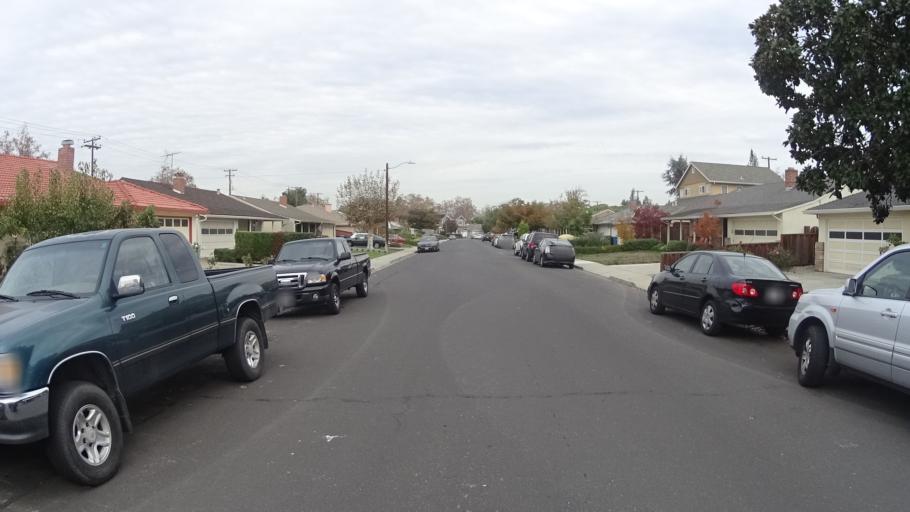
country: US
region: California
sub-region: Santa Clara County
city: Santa Clara
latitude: 37.3340
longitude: -121.9568
